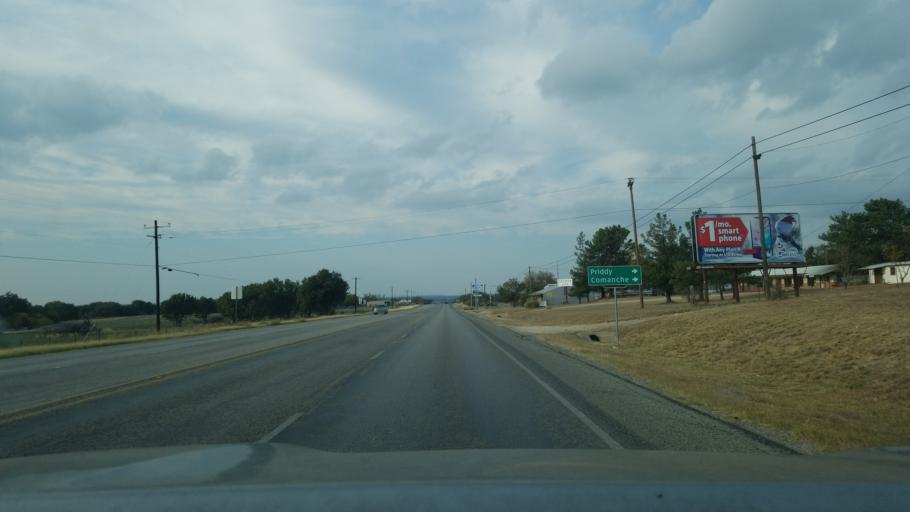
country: US
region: Texas
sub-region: Mills County
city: Goldthwaite
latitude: 31.4827
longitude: -98.5712
